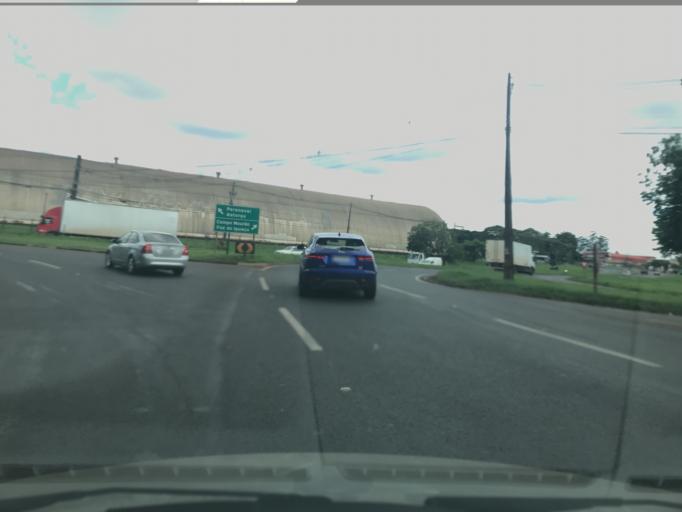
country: BR
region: Parana
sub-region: Maringa
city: Maringa
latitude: -23.4223
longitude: -51.9746
